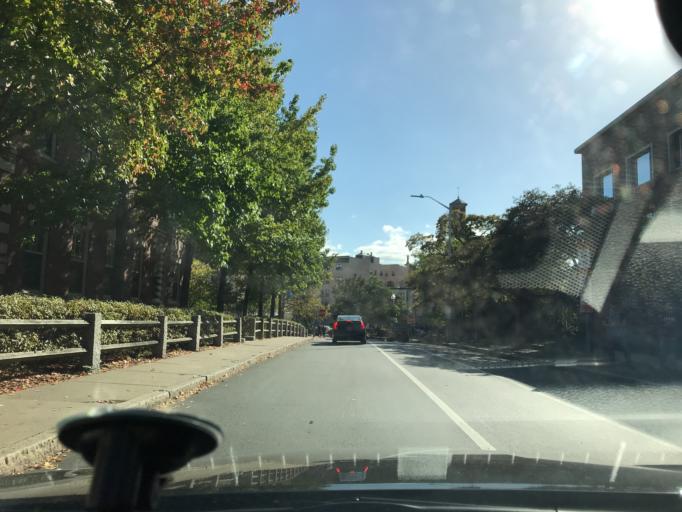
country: US
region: Massachusetts
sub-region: Middlesex County
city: Cambridge
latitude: 42.3730
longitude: -71.1150
